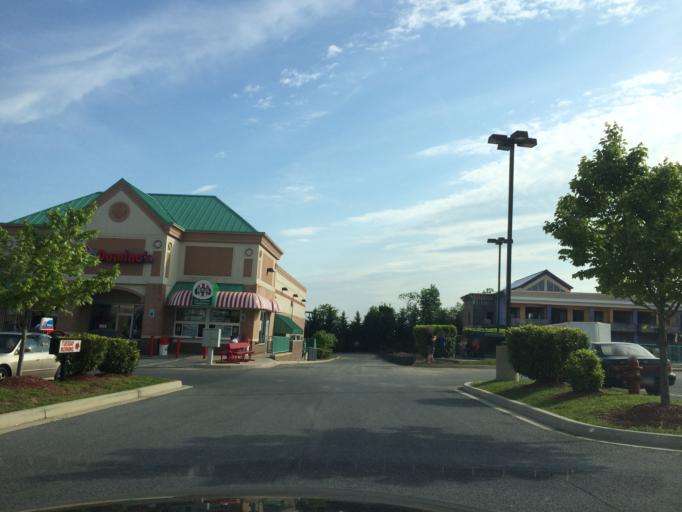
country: US
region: Maryland
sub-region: Carroll County
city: Eldersburg
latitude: 39.4037
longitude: -76.9528
